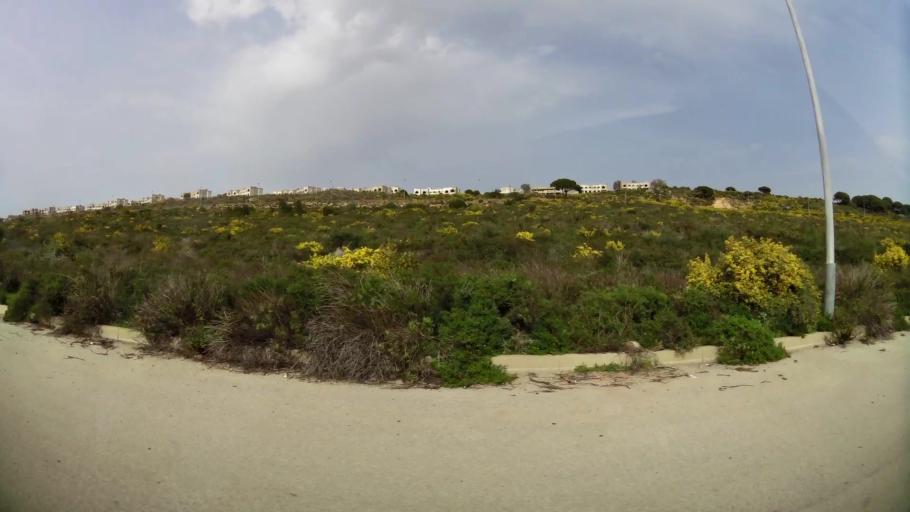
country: MA
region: Tanger-Tetouan
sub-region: Tanger-Assilah
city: Boukhalef
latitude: 35.6922
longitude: -5.9397
